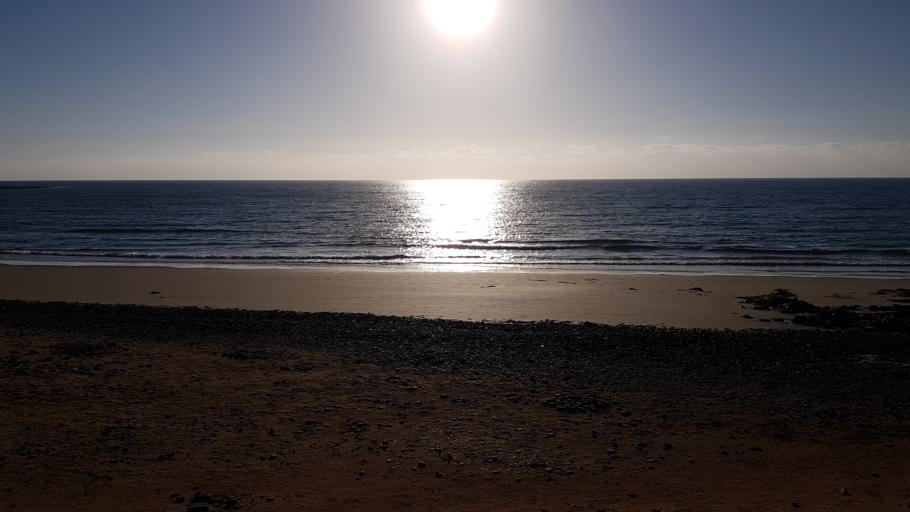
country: ES
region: Canary Islands
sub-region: Provincia de Las Palmas
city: Pajara
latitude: 28.1645
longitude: -14.2204
